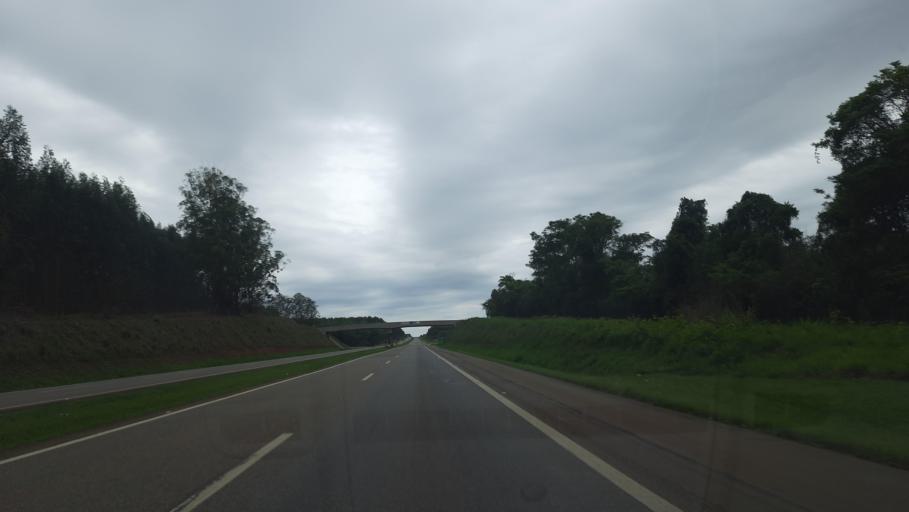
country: BR
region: Sao Paulo
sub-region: Casa Branca
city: Casa Branca
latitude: -21.8553
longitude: -47.0635
